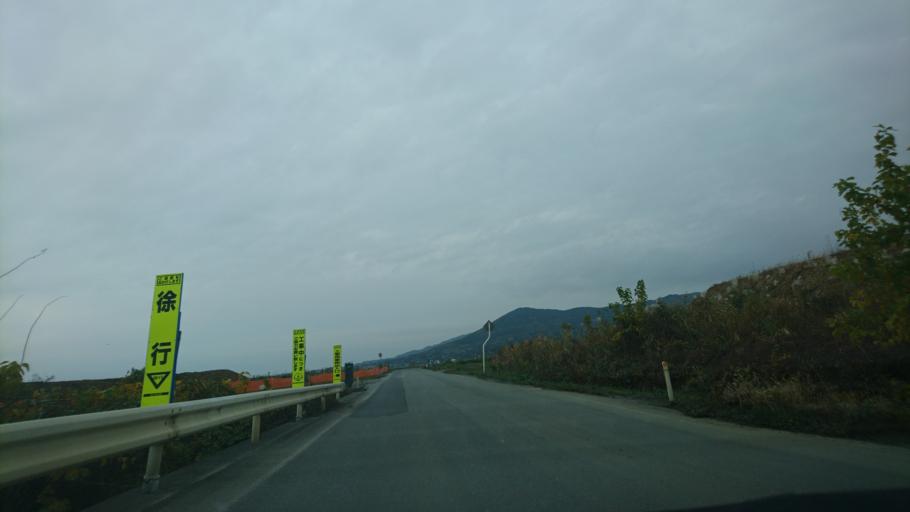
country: JP
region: Iwate
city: Ichinoseki
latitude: 38.9511
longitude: 141.1695
